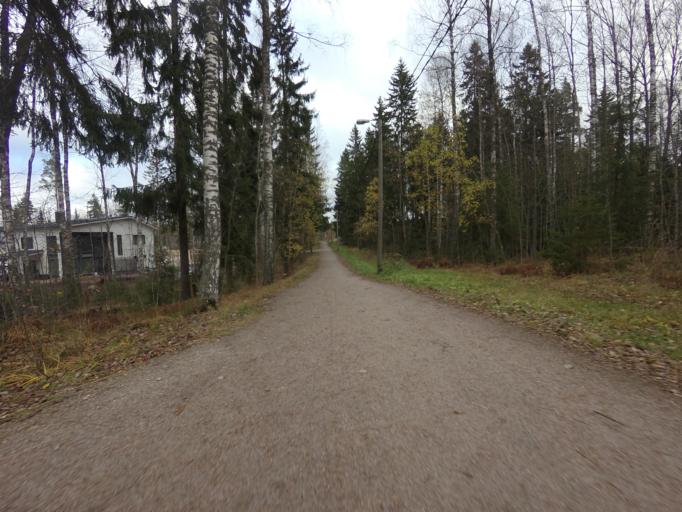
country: FI
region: Uusimaa
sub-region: Helsinki
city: Kauniainen
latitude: 60.1971
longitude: 24.7009
